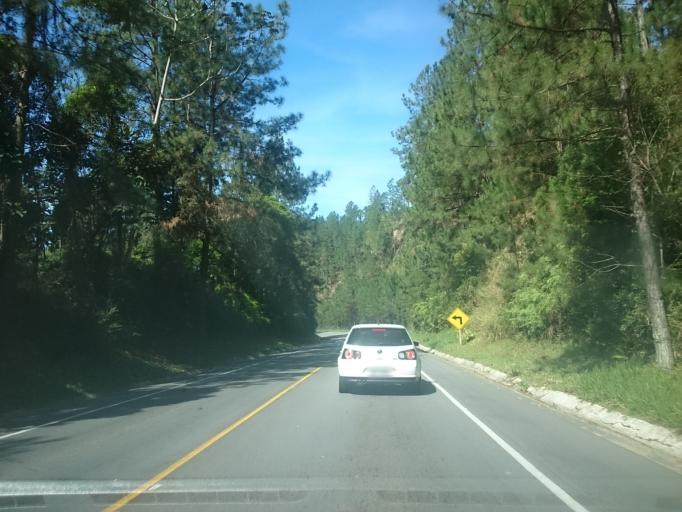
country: BR
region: Santa Catarina
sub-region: Santo Amaro Da Imperatriz
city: Santo Amaro da Imperatriz
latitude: -27.7216
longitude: -48.9082
